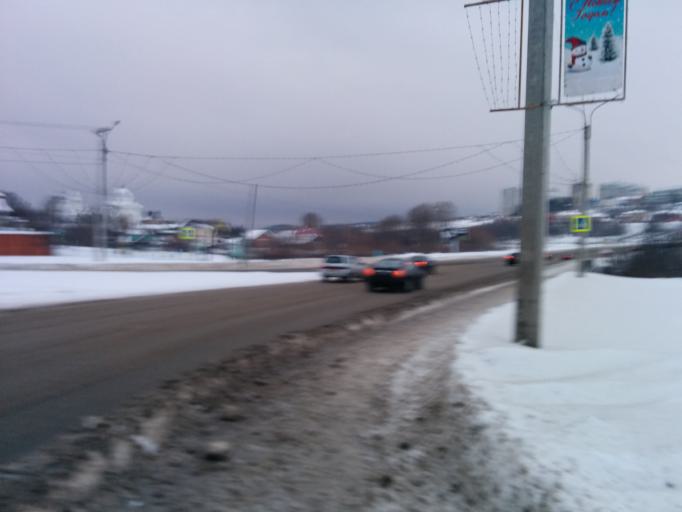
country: RU
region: Chuvashia
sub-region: Cheboksarskiy Rayon
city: Cheboksary
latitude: 56.1370
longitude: 47.2365
